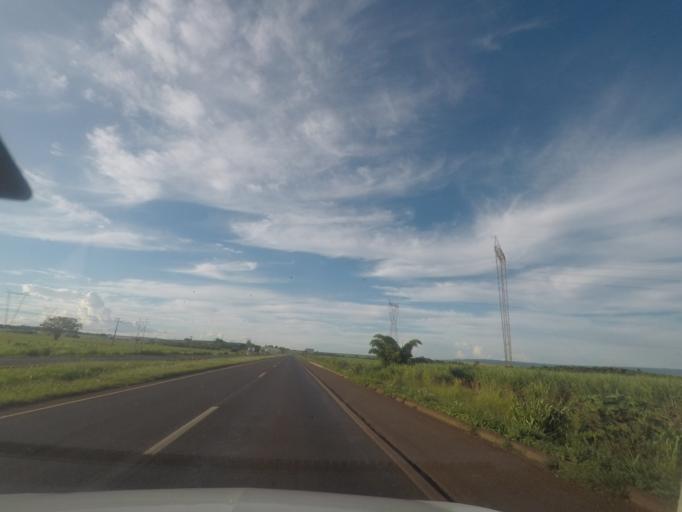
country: BR
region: Goias
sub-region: Itumbiara
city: Itumbiara
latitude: -18.3321
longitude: -49.2250
